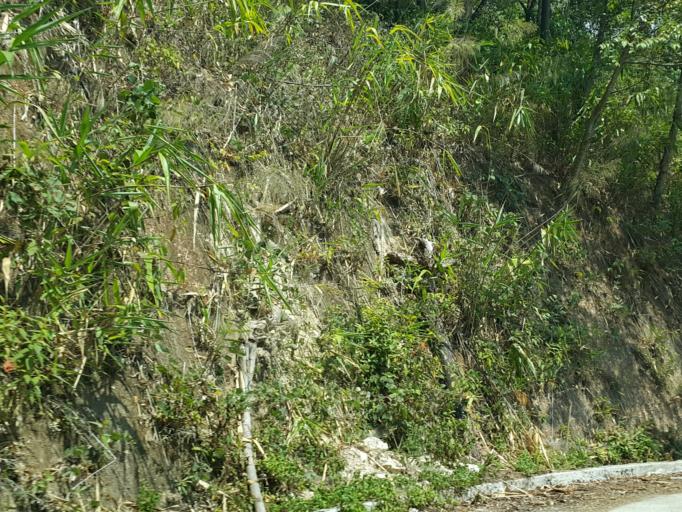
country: TH
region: Chiang Mai
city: Mae On
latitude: 18.8540
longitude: 99.3699
